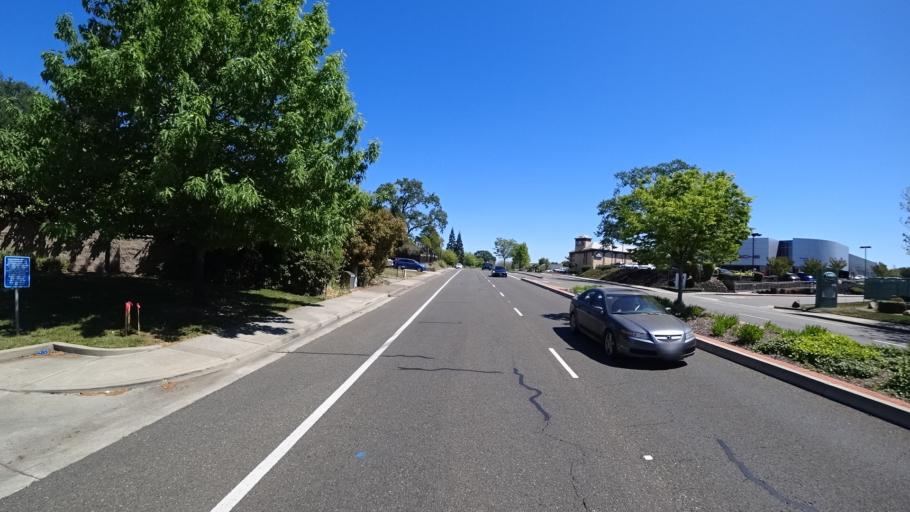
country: US
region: California
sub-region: Placer County
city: Rocklin
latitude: 38.7929
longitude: -121.2206
